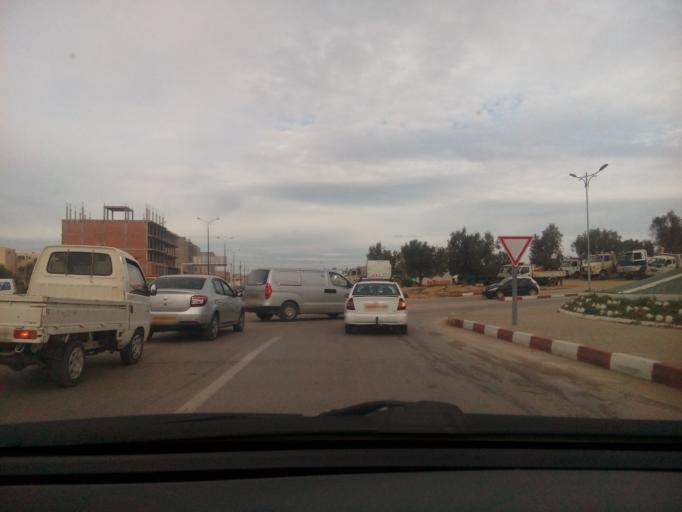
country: DZ
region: Tlemcen
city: Mansoura
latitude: 34.8845
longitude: -1.3518
